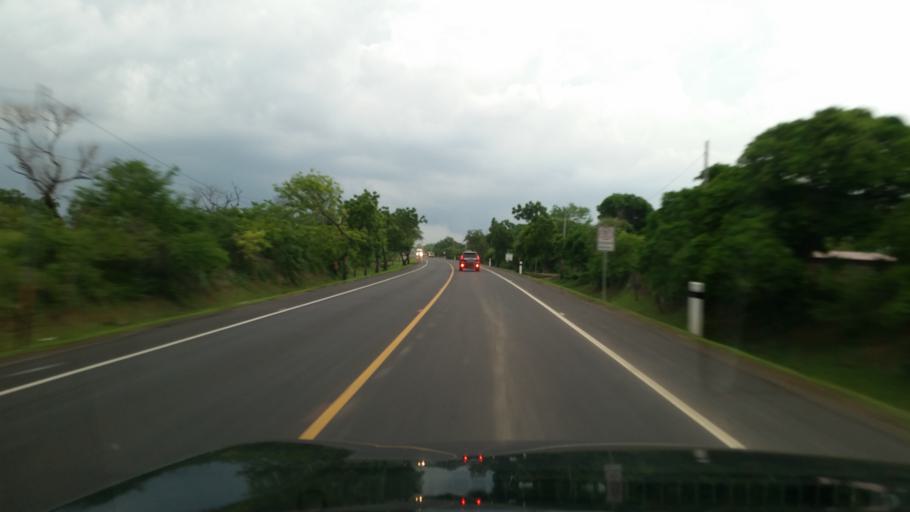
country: NI
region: Leon
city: Nagarote
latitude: 12.2753
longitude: -86.5730
